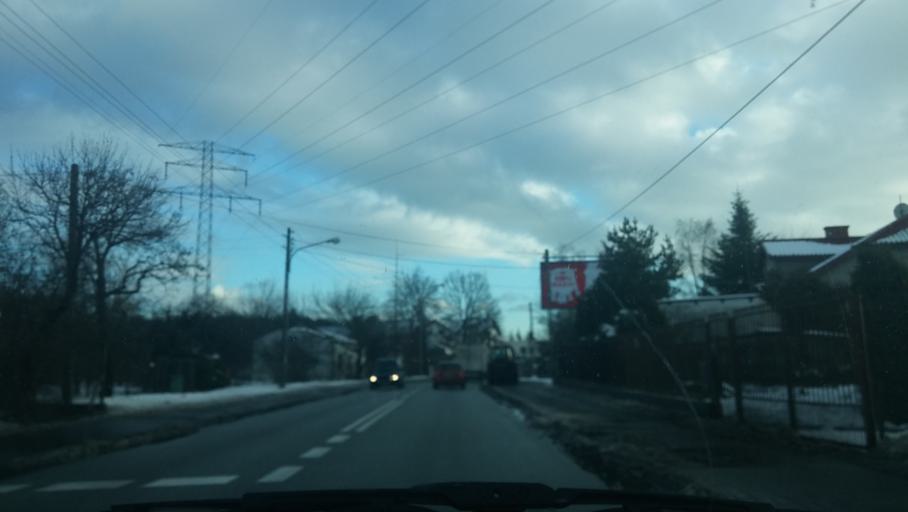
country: PL
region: Masovian Voivodeship
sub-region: Warszawa
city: Rembertow
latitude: 52.2514
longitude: 21.1296
